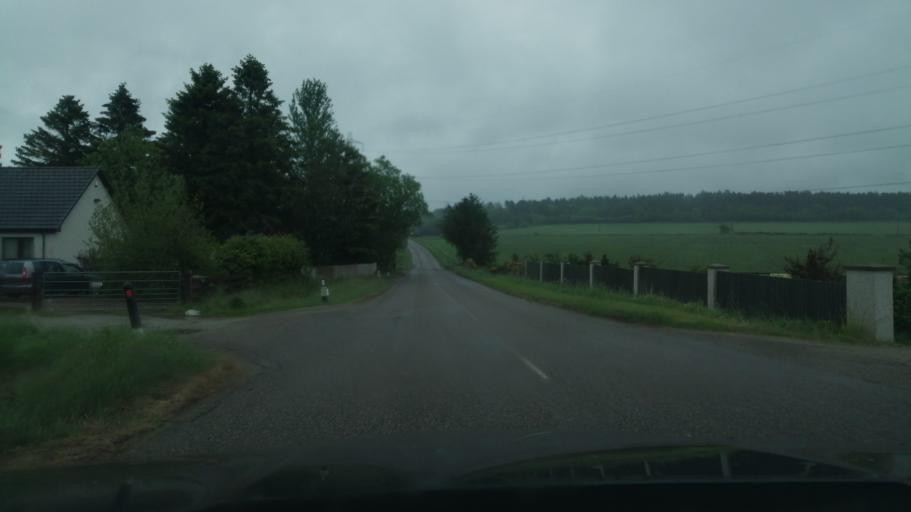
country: GB
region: Scotland
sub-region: Aberdeenshire
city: Huntly
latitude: 57.5454
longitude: -2.8105
